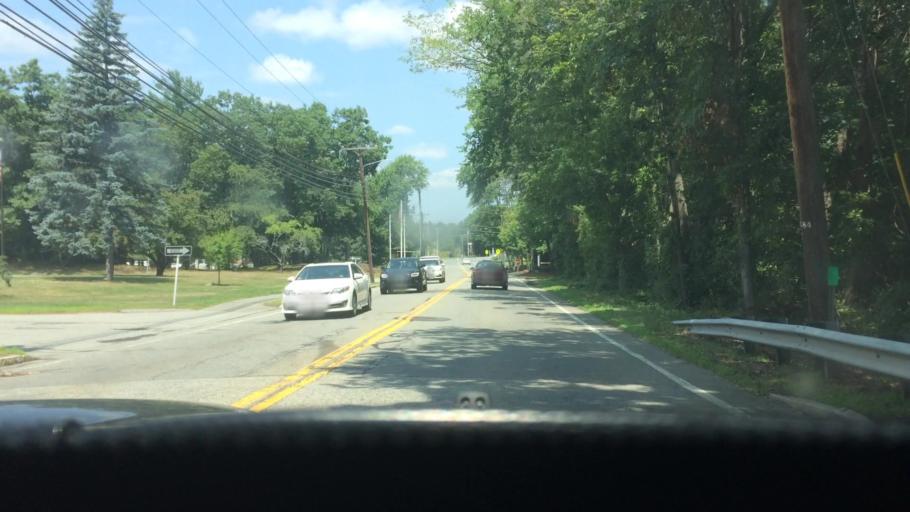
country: US
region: Massachusetts
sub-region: Middlesex County
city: Chelmsford
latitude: 42.6172
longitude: -71.3645
